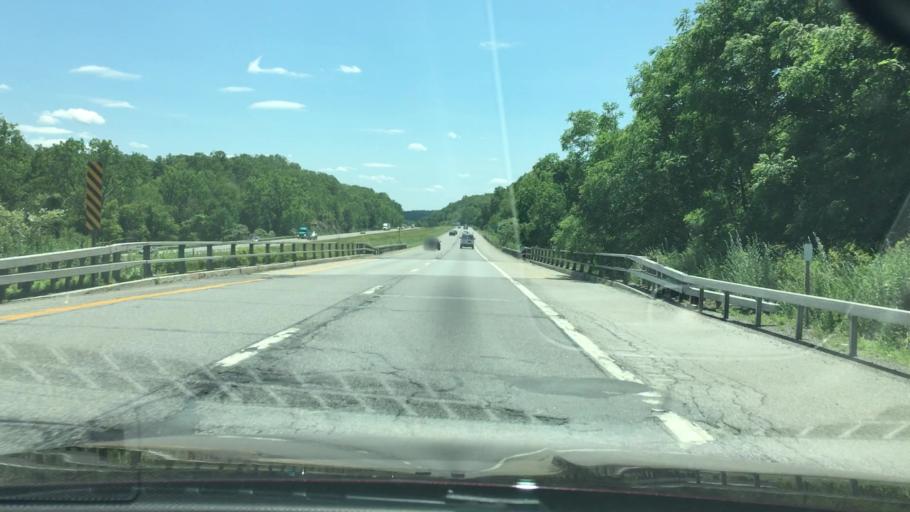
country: US
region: New York
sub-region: Putnam County
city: Lake Carmel
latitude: 41.4656
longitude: -73.6448
